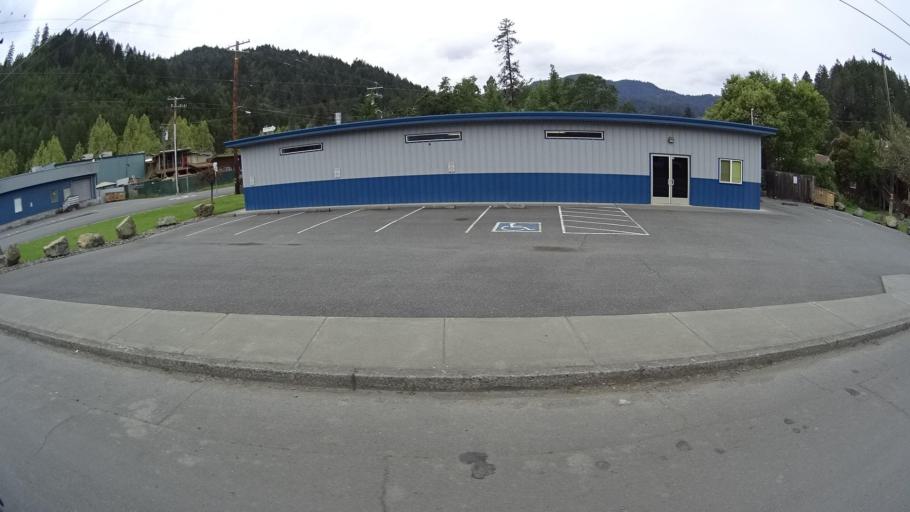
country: US
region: California
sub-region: Humboldt County
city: Willow Creek
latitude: 40.9399
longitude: -123.6295
